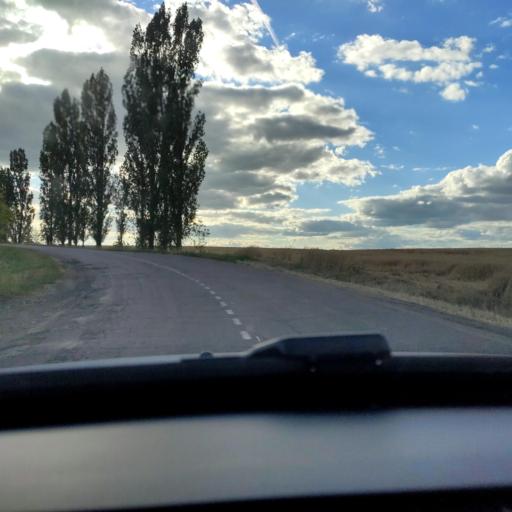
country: RU
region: Voronezj
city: Orlovo
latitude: 51.6160
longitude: 39.8055
